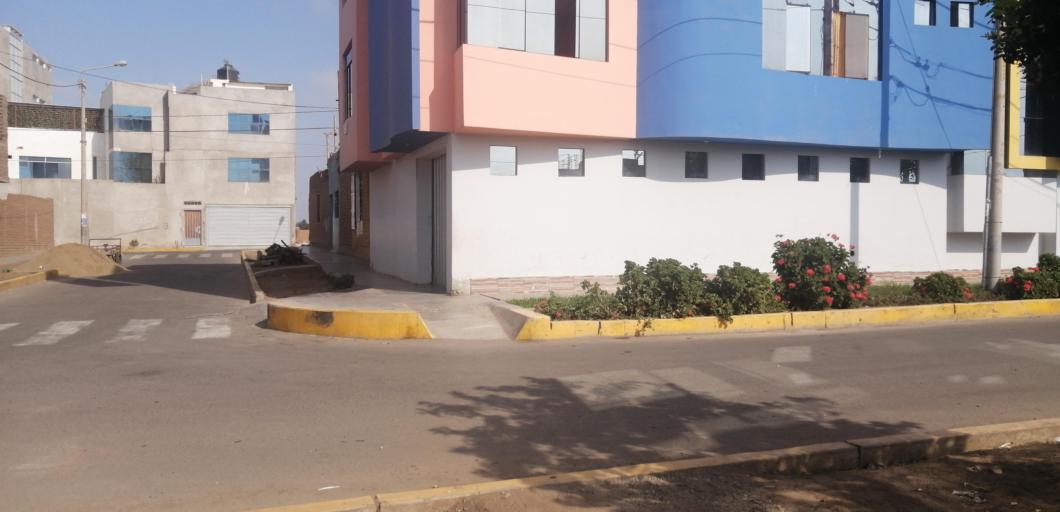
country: PE
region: La Libertad
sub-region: Provincia de Trujillo
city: Trujillo
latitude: -8.1077
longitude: -79.0478
